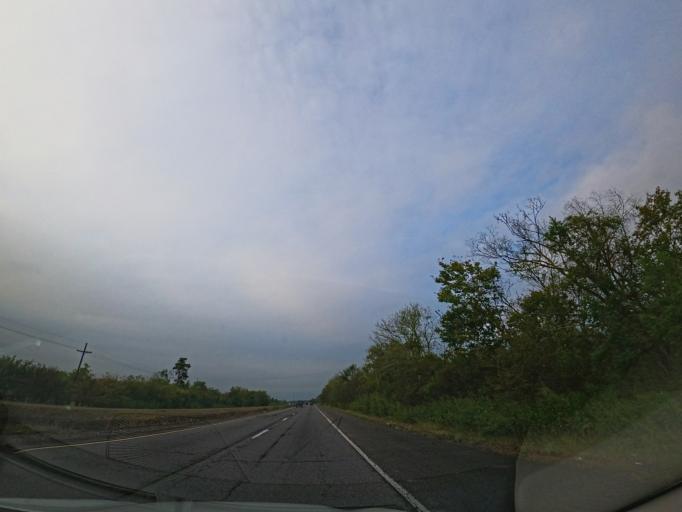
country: US
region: Louisiana
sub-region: Terrebonne Parish
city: Houma
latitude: 29.6650
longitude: -90.6694
